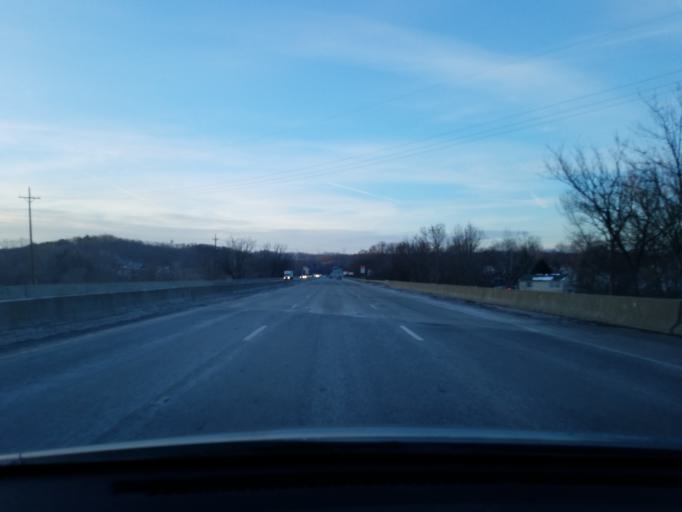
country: US
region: Indiana
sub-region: Floyd County
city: New Albany
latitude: 38.2904
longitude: -85.8346
